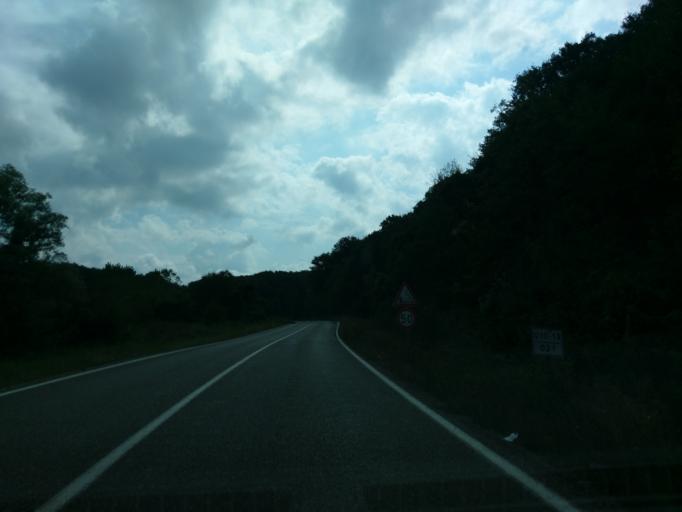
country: TR
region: Sinop
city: Yenikonak
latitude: 41.9465
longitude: 34.7470
